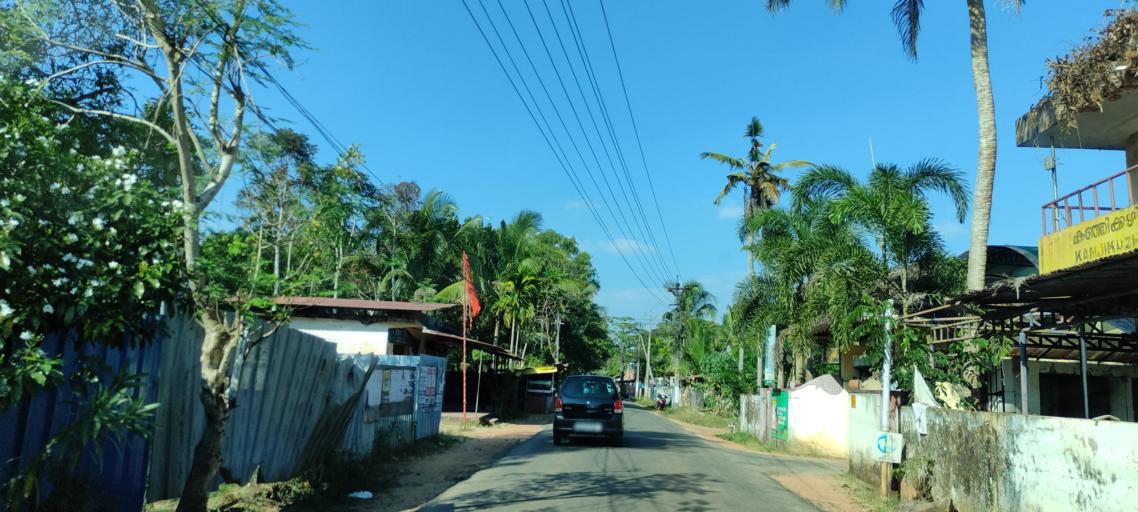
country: IN
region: Kerala
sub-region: Alappuzha
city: Shertallai
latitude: 9.6220
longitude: 76.3425
